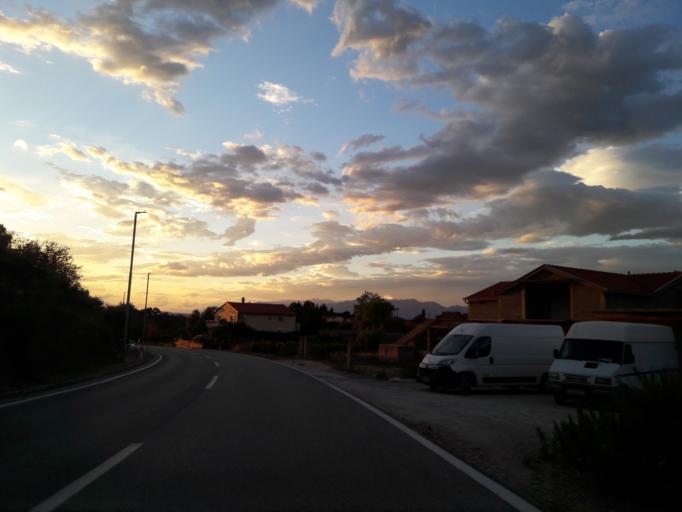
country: HR
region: Dubrovacko-Neretvanska
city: Orebic
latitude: 43.0037
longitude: 17.2759
